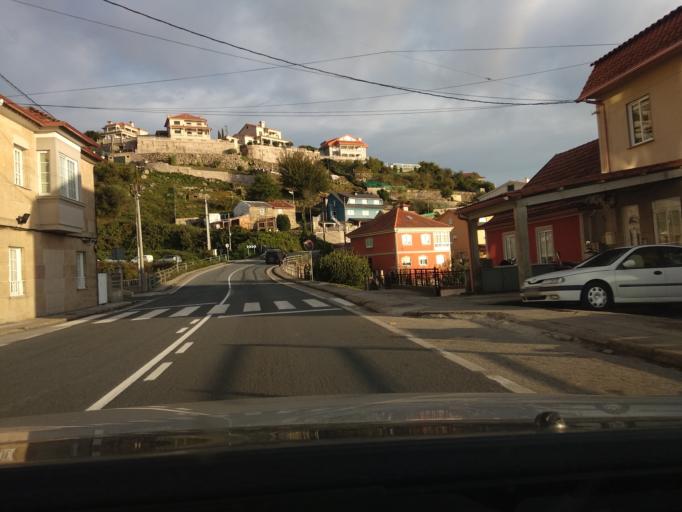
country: ES
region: Galicia
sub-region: Provincia de Pontevedra
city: Moana
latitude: 42.2846
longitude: -8.7143
